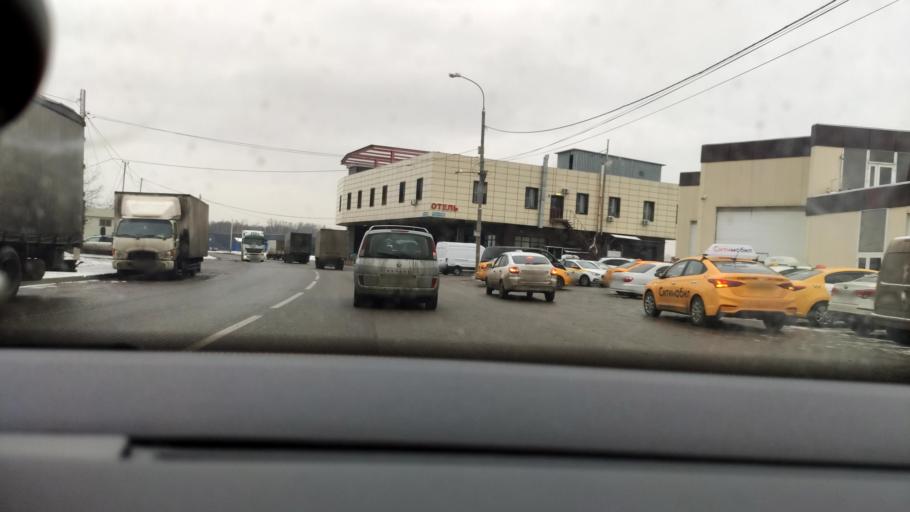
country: RU
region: Moscow
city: Khimki
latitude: 55.9184
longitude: 37.4220
